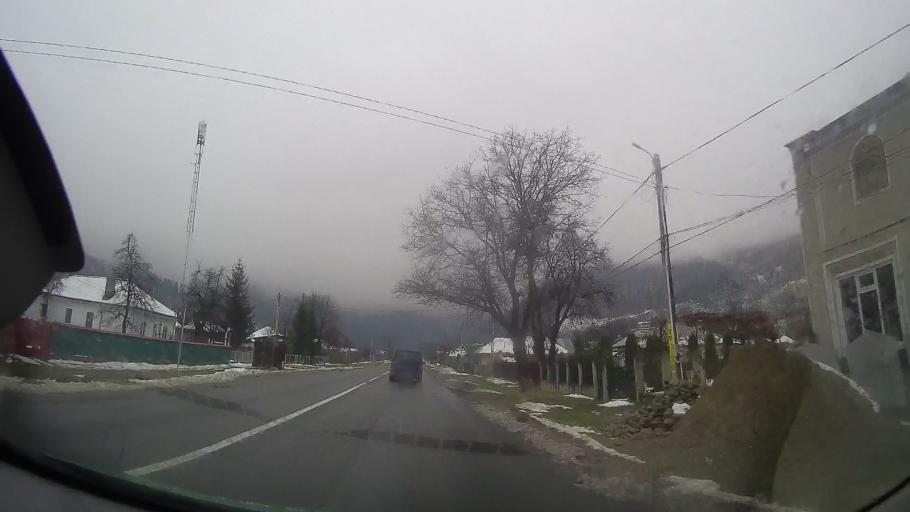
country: RO
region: Neamt
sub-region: Comuna Pangarati
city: Stejaru
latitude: 46.9004
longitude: 26.1728
